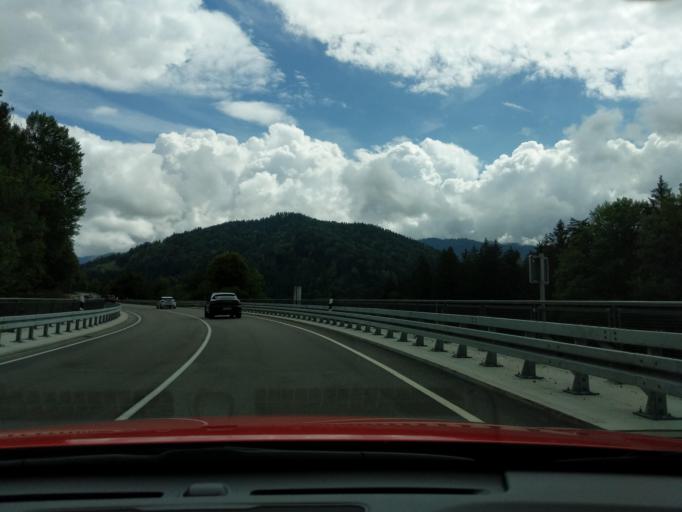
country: DE
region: Bavaria
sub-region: Swabia
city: Oberstaufen
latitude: 47.5491
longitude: 10.0280
